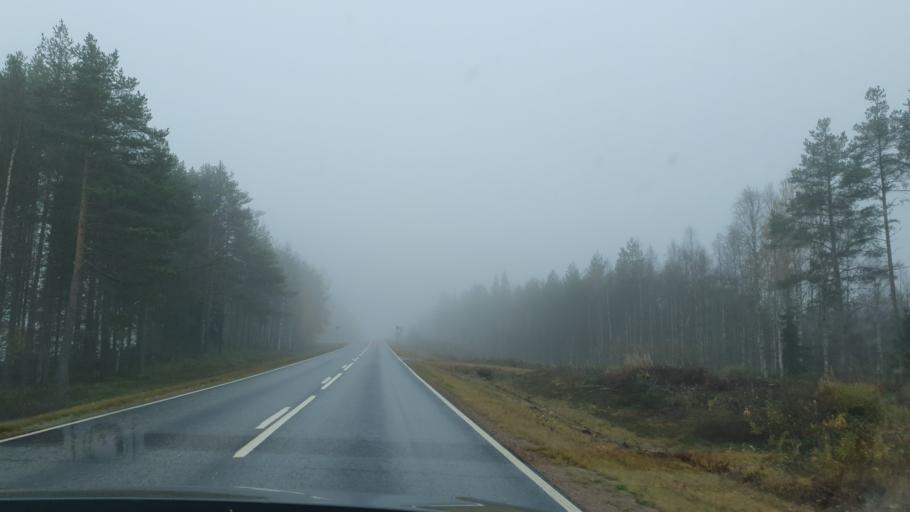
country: FI
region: Lapland
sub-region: Rovaniemi
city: Rovaniemi
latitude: 66.7931
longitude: 25.4155
